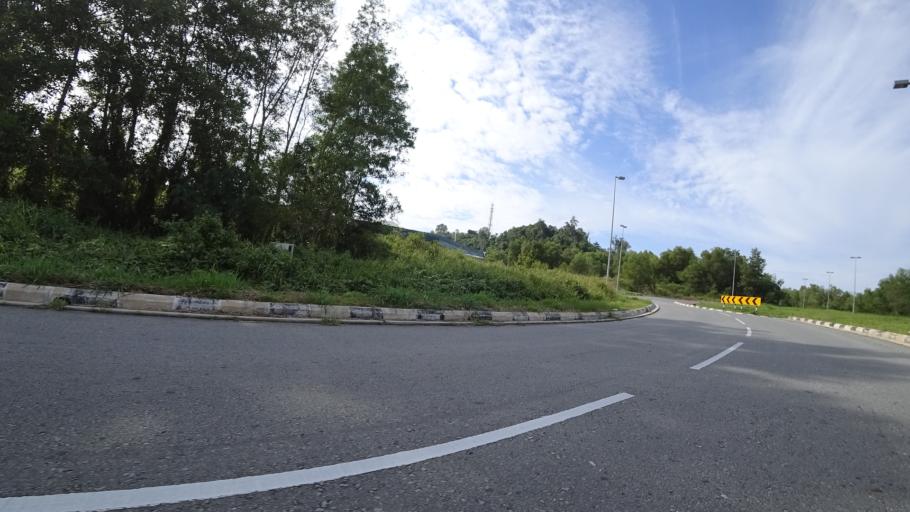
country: BN
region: Brunei and Muara
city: Bandar Seri Begawan
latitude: 4.8966
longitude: 114.8032
